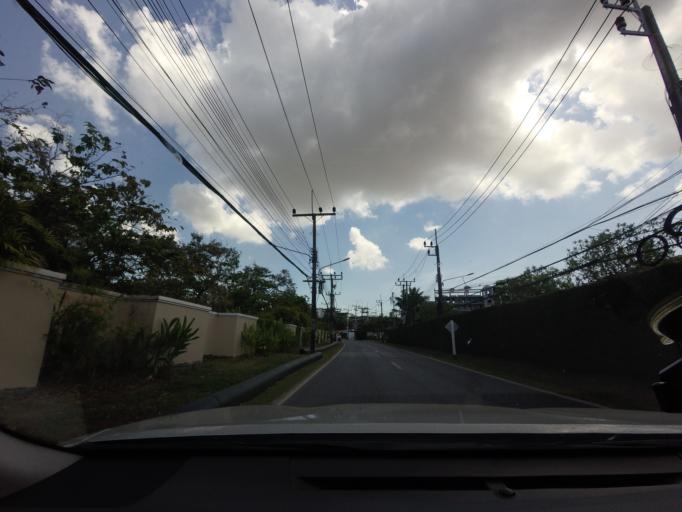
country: TH
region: Phuket
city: Thalang
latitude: 8.0186
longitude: 98.3044
